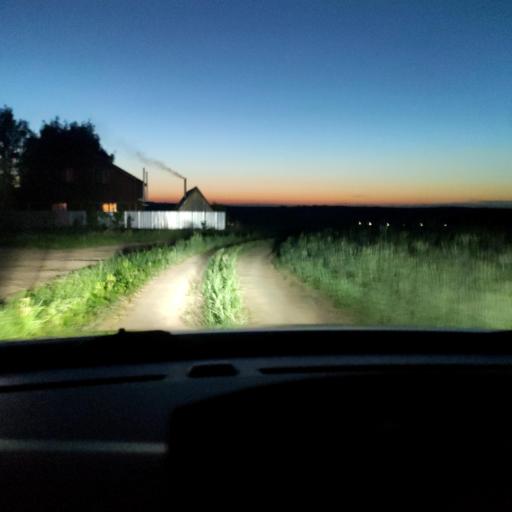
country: RU
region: Tatarstan
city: Vysokaya Gora
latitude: 55.8453
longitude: 49.3329
